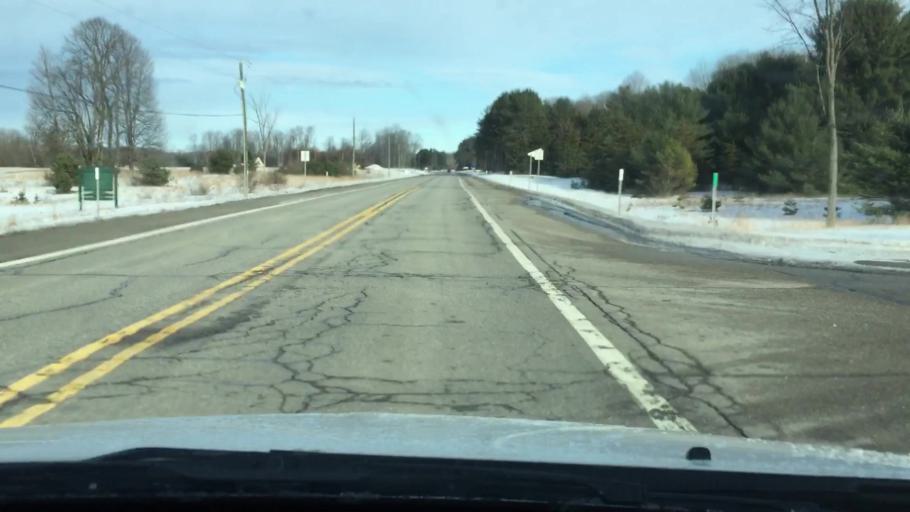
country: US
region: Michigan
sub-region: Wexford County
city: Manton
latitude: 44.5868
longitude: -85.3504
